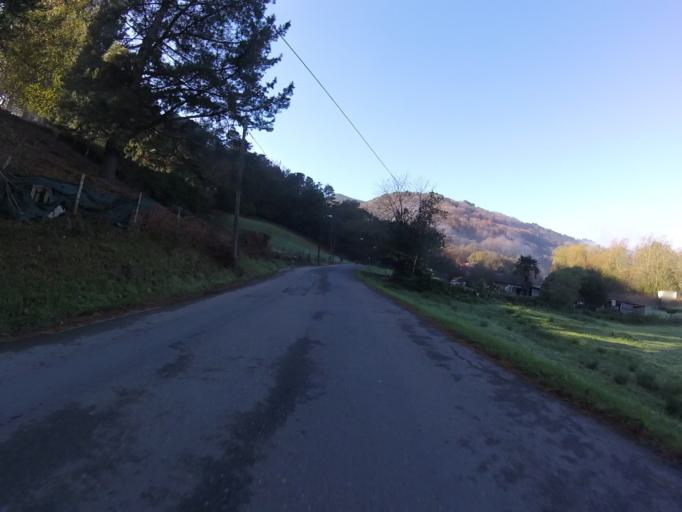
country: ES
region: Basque Country
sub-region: Provincia de Guipuzcoa
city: Usurbil
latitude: 43.2629
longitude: -2.0459
